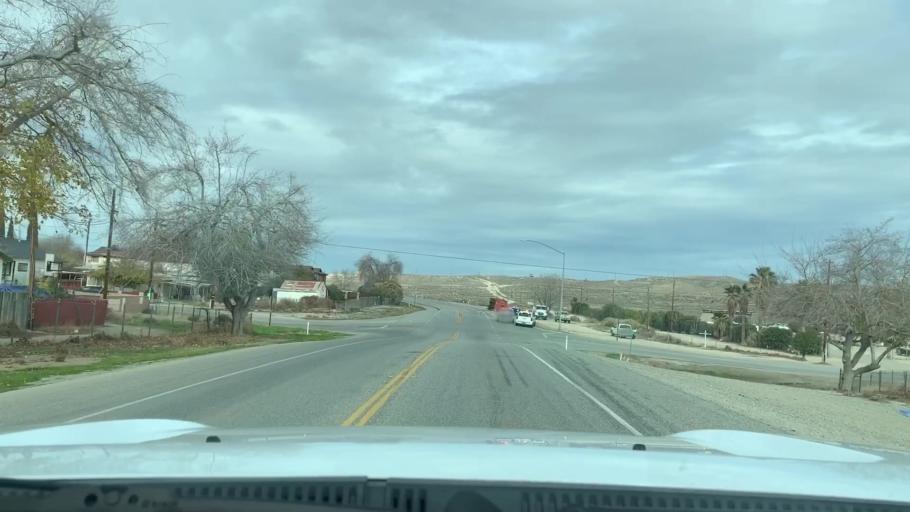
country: US
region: California
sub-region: Kern County
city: Ford City
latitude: 35.1540
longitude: -119.4479
